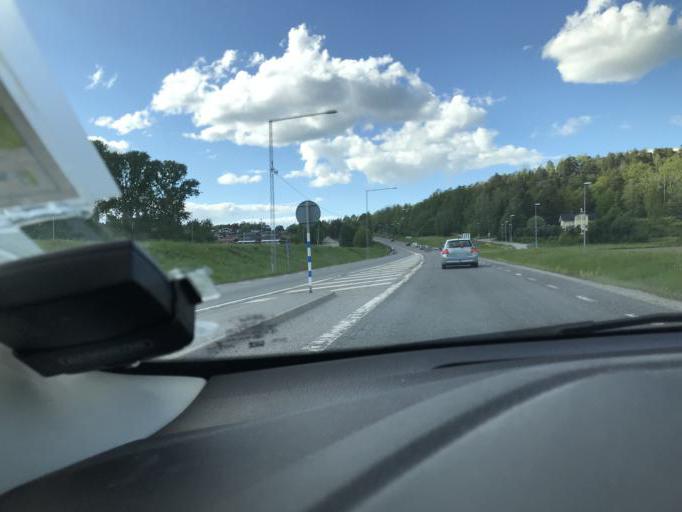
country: SE
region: Stockholm
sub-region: Botkyrka Kommun
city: Tumba
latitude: 59.2041
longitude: 17.8413
